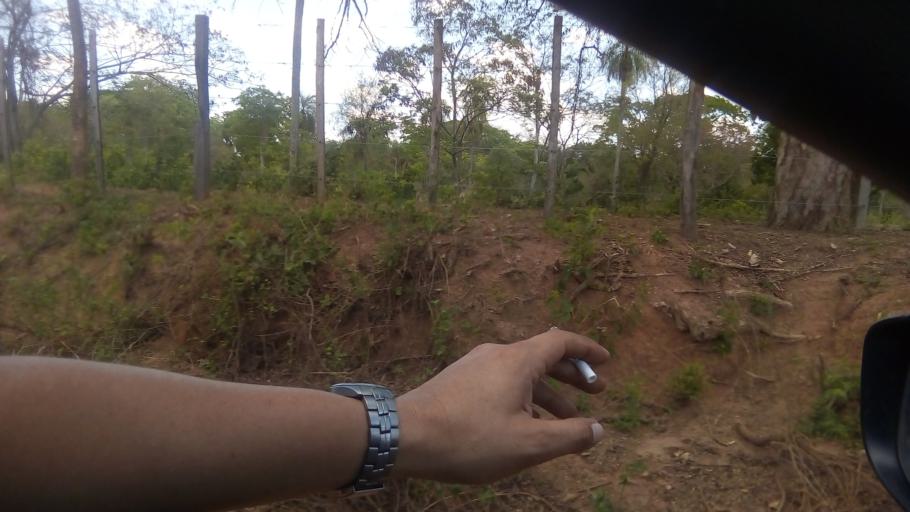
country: PY
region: Cordillera
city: Arroyos y Esteros
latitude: -24.9885
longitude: -57.2112
